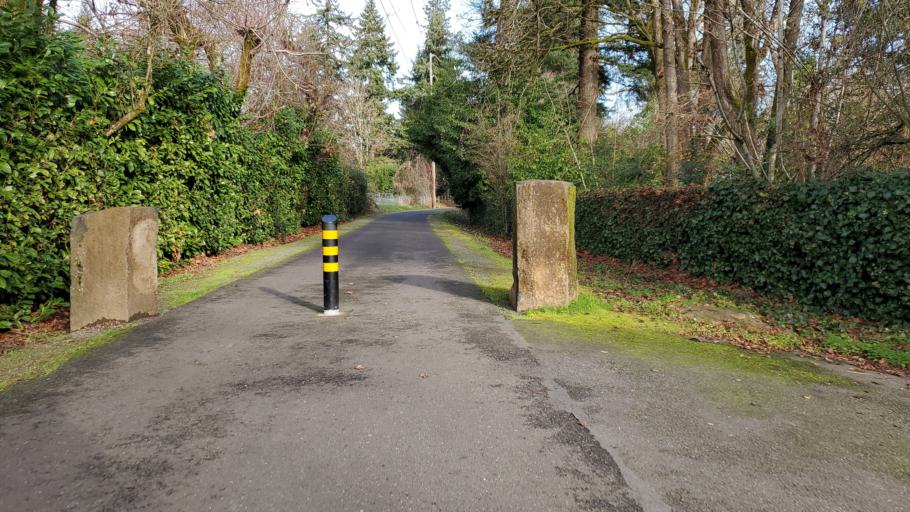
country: US
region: Oregon
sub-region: Clackamas County
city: Oak Grove
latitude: 45.4276
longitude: -122.6385
